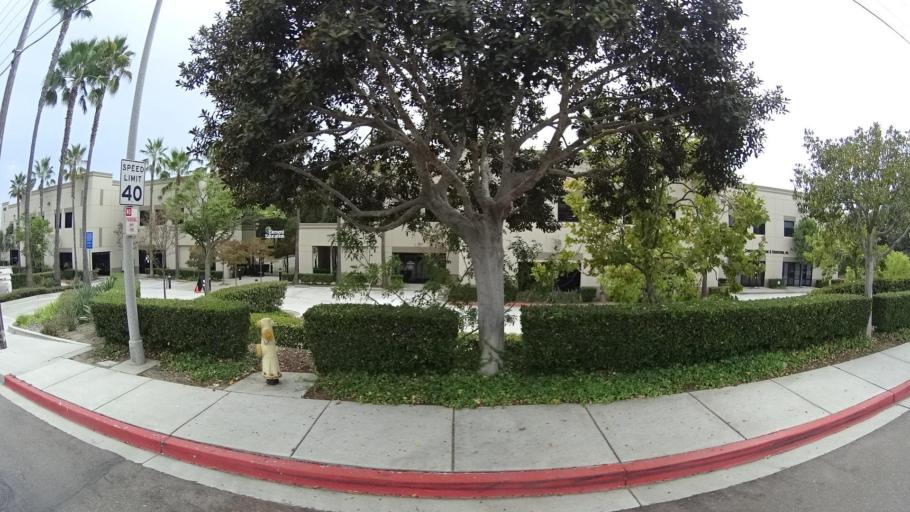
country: US
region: California
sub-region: San Diego County
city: Escondido
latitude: 33.1299
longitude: -117.1122
